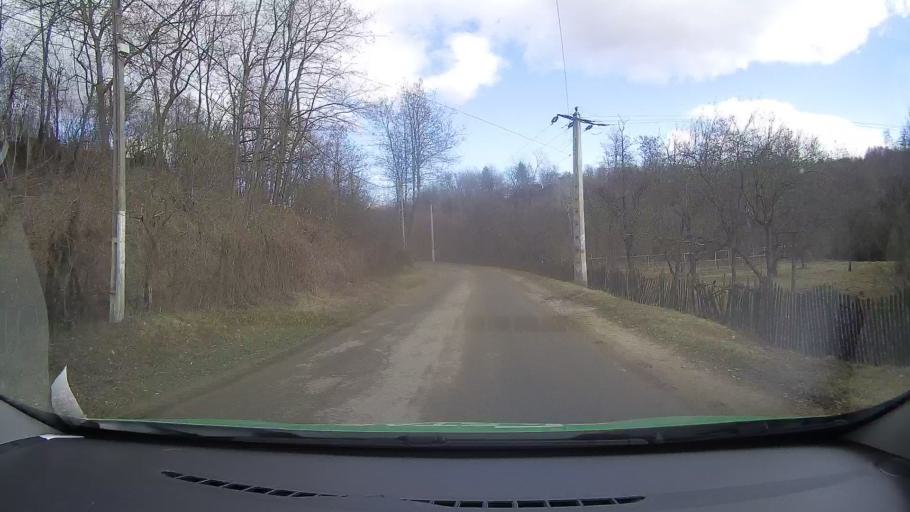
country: RO
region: Dambovita
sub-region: Comuna Buciumeni
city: Buciumeni
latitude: 45.1297
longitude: 25.4677
